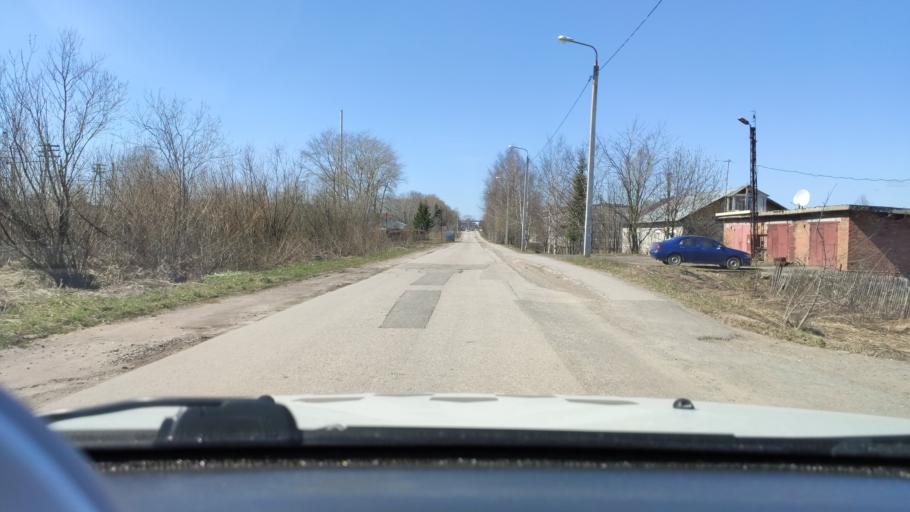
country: RU
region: Perm
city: Novyye Lyady
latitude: 58.0470
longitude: 56.6091
